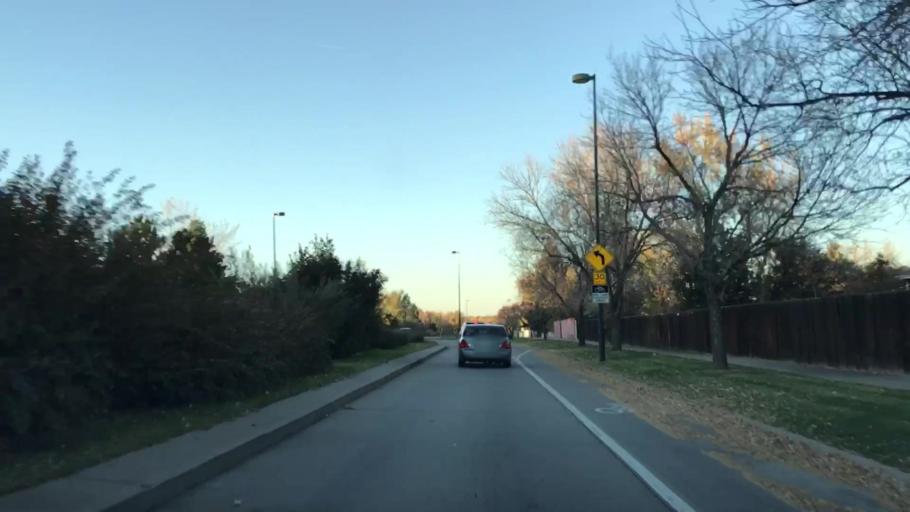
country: US
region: Colorado
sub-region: Arapahoe County
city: Glendale
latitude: 39.6590
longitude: -104.8846
